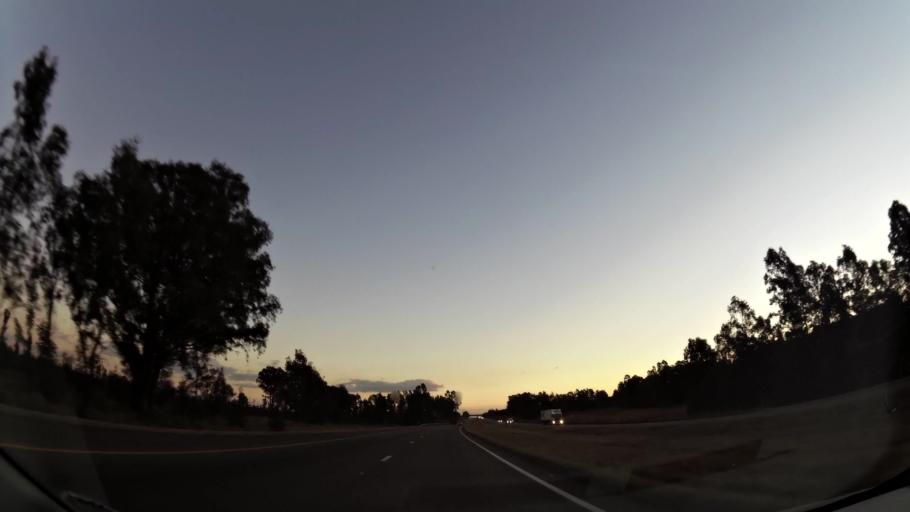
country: ZA
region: Mpumalanga
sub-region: Nkangala District Municipality
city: Witbank
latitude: -25.9682
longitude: 29.1878
